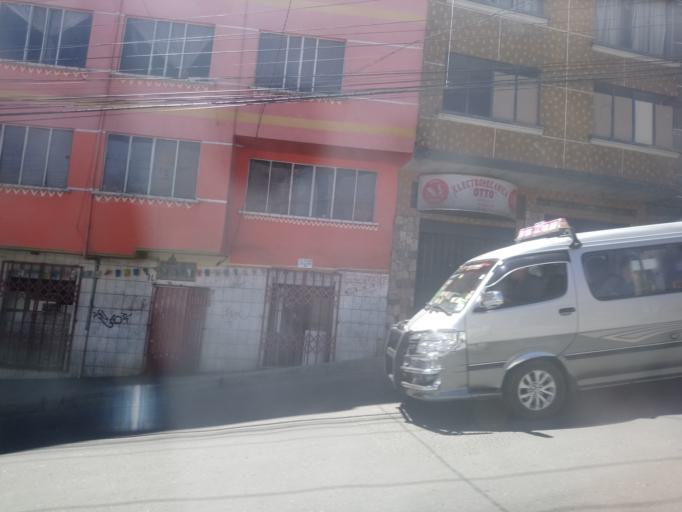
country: BO
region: La Paz
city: La Paz
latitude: -16.4952
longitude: -68.1107
